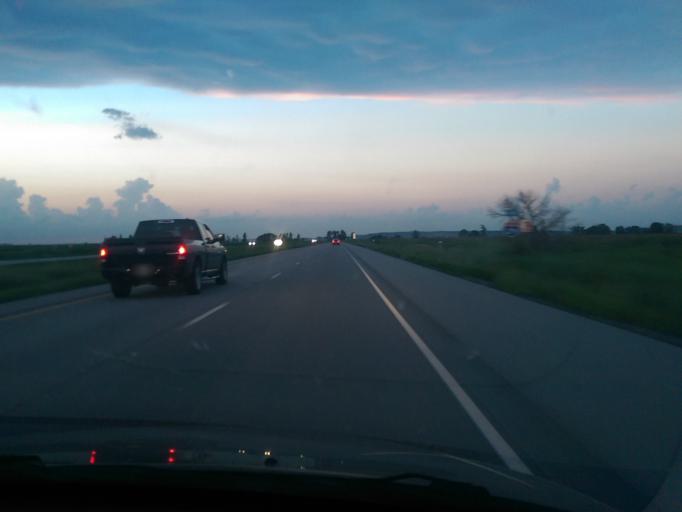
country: US
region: Nebraska
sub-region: Otoe County
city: Nebraska City
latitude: 40.7656
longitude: -95.8136
